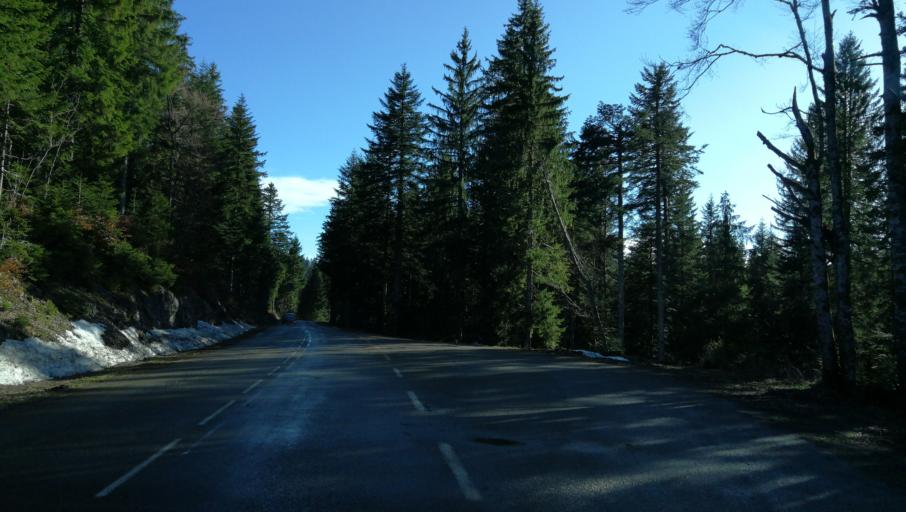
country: FR
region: Franche-Comte
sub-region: Departement du Jura
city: Saint-Claude
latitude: 46.2721
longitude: 5.8260
